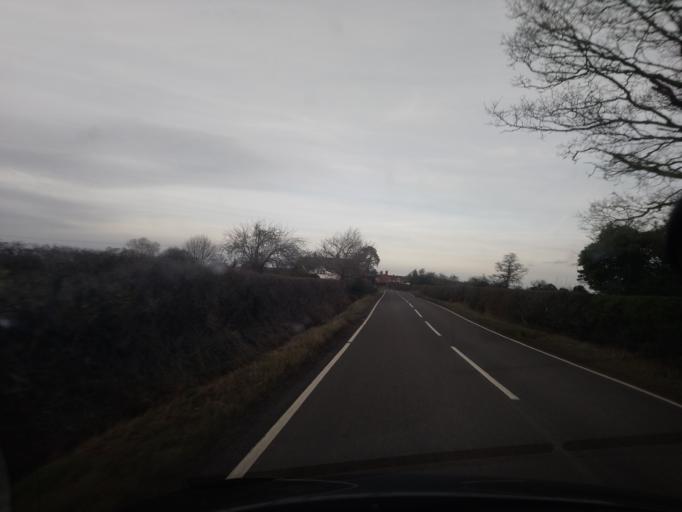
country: GB
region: England
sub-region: Shropshire
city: Prees
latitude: 52.9175
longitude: -2.6825
